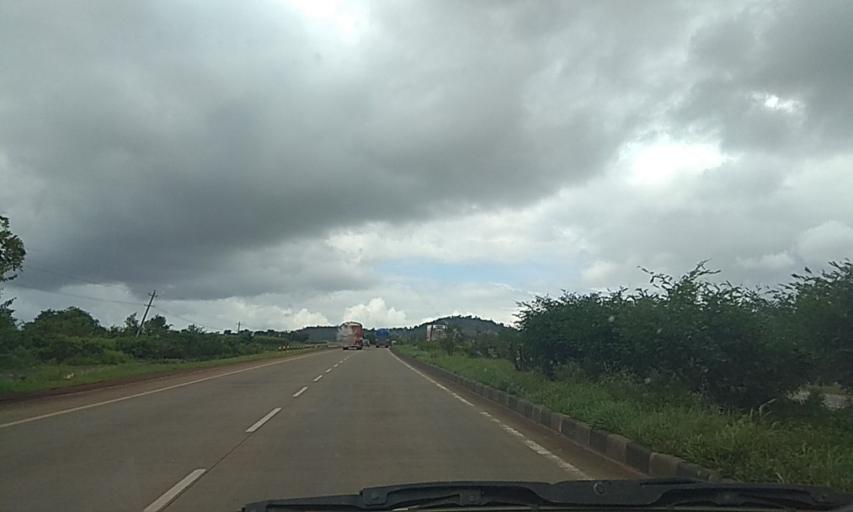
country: IN
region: Karnataka
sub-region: Belgaum
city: Sankeshwar
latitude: 16.2598
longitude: 74.4675
